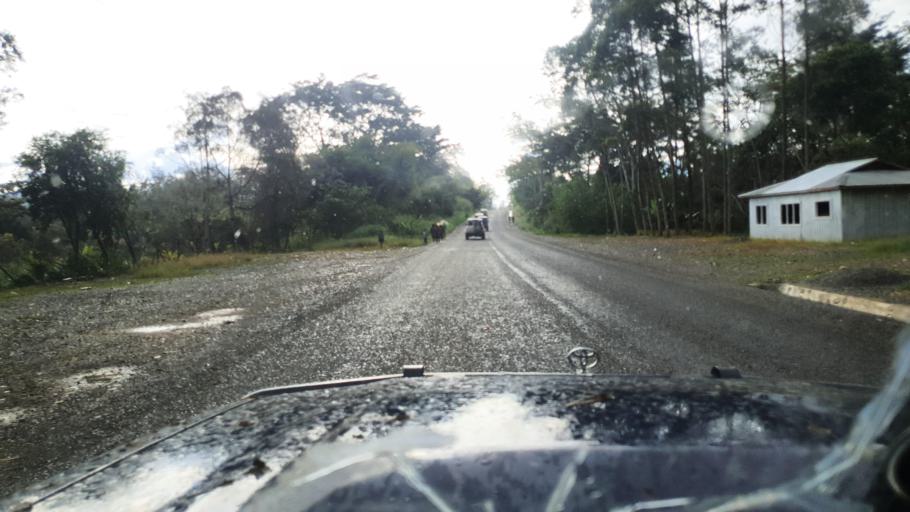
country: PG
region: Jiwaka
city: Minj
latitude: -5.9258
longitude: 144.7869
